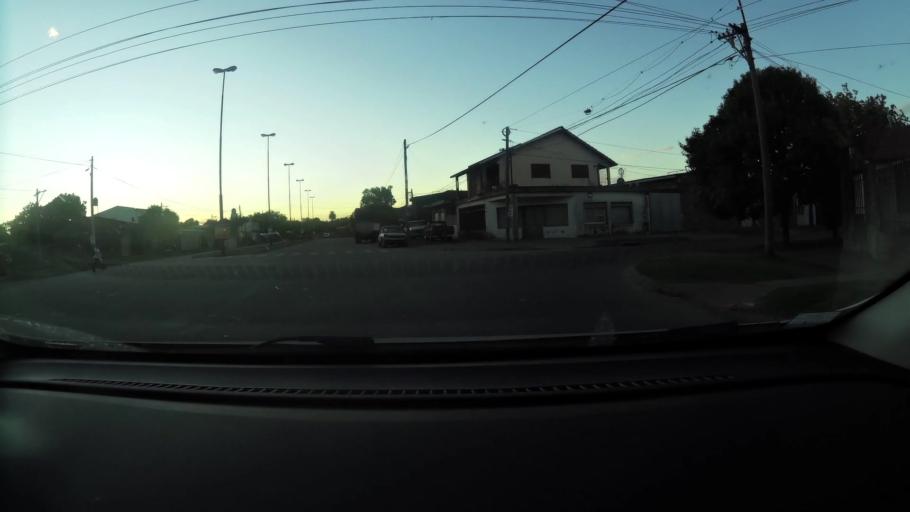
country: AR
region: Santa Fe
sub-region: Departamento de Rosario
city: Rosario
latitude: -32.9715
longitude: -60.6886
